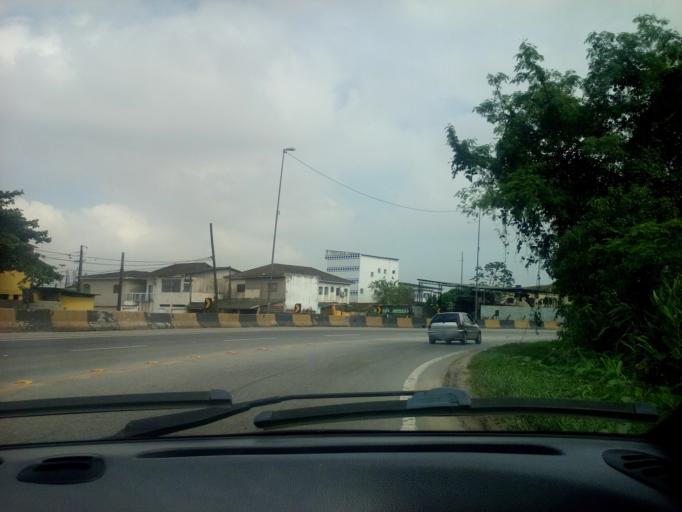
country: BR
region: Sao Paulo
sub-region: Guaruja
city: Guaruja
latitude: -23.9696
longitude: -46.2722
